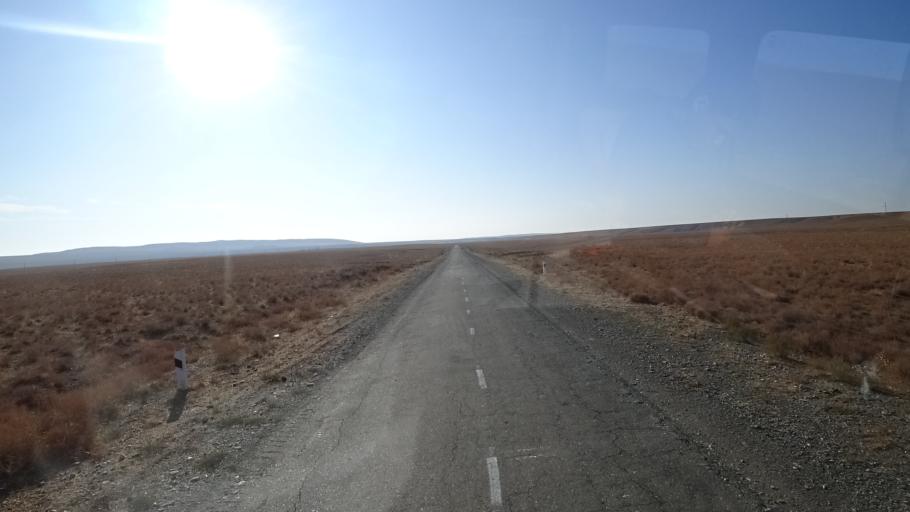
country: UZ
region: Navoiy
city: Karmana Shahri
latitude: 40.2637
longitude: 65.5042
